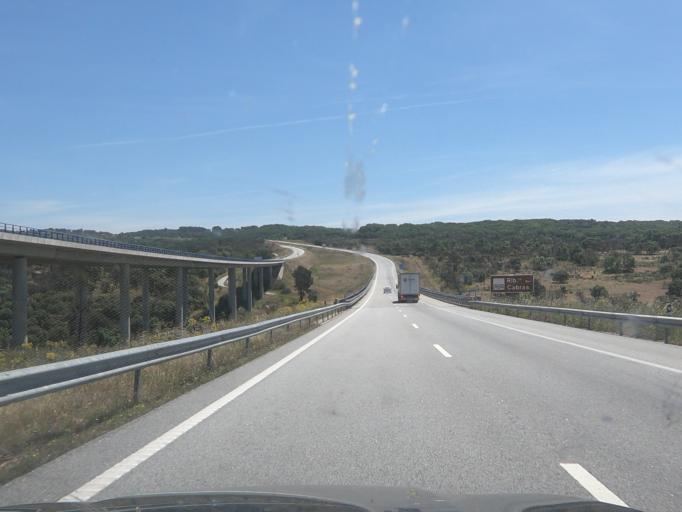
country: PT
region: Guarda
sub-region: Pinhel
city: Pinhel
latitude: 40.6046
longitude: -7.0338
